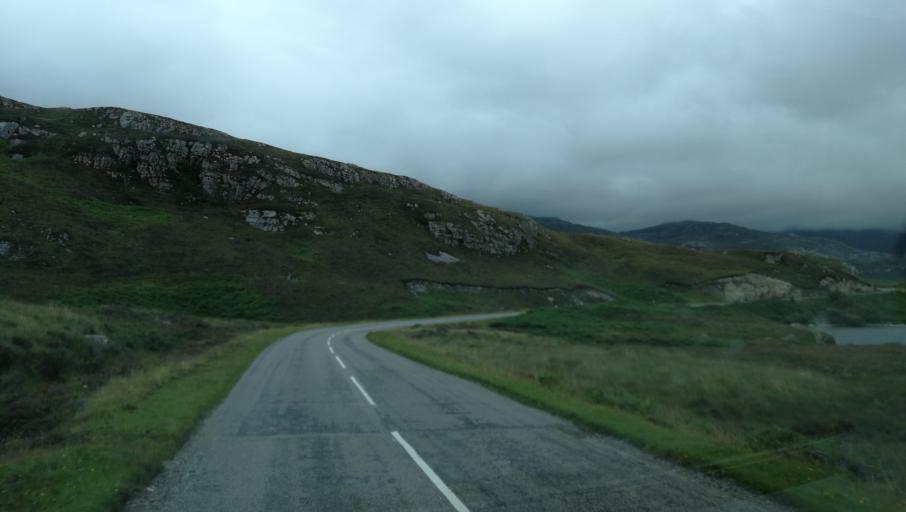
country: GB
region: Scotland
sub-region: Highland
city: Ullapool
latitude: 58.1756
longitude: -5.0161
